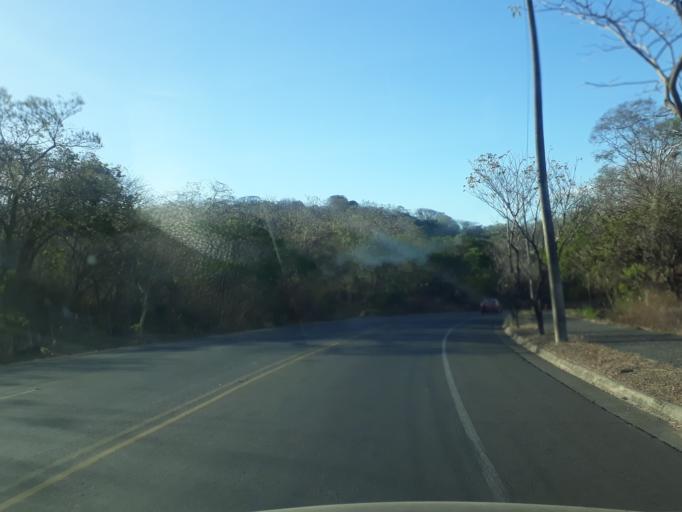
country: CR
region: Puntarenas
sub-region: Canton Central de Puntarenas
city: Chacarita
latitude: 9.9450
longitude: -84.7273
